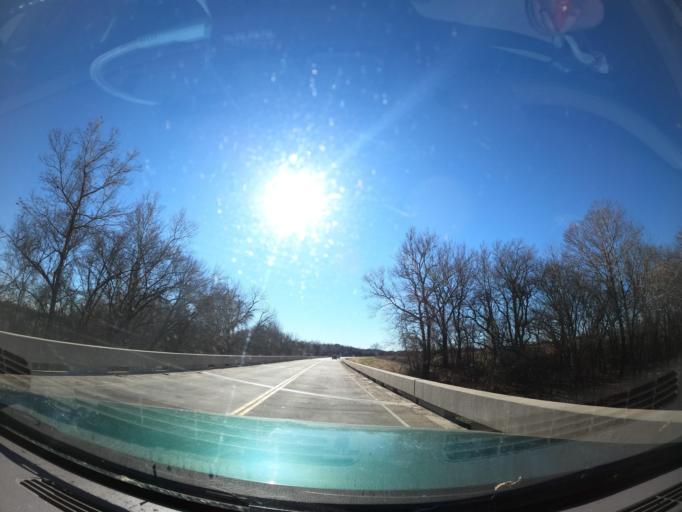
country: US
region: Oklahoma
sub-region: Muskogee County
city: Haskell
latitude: 35.8780
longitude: -95.6618
